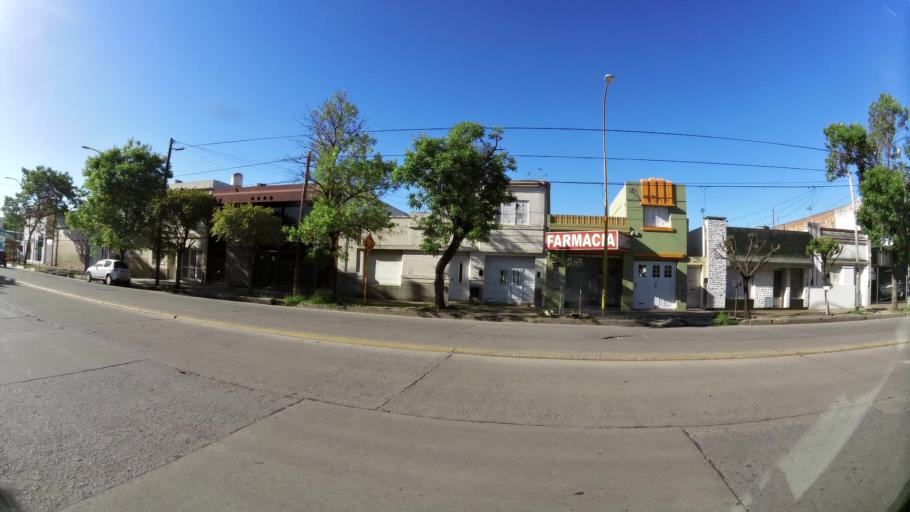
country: AR
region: Cordoba
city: San Francisco
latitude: -31.4291
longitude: -62.0965
